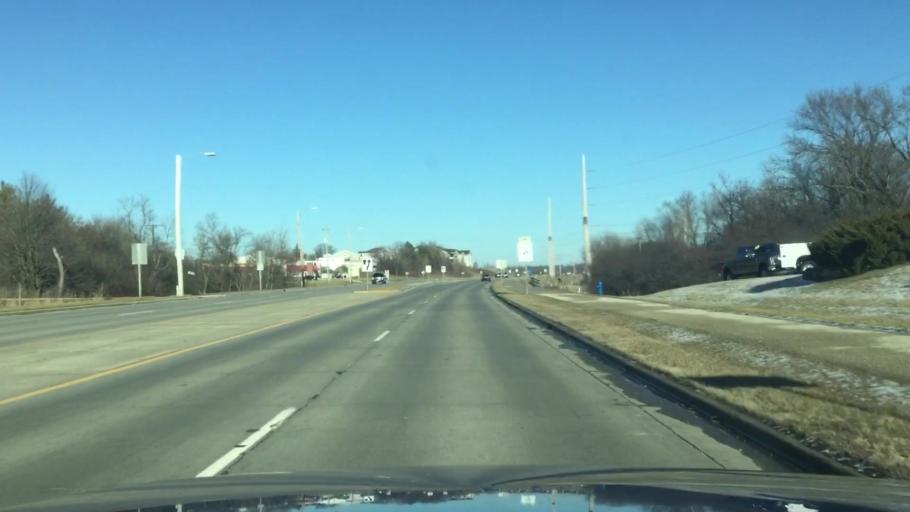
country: US
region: Wisconsin
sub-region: Racine County
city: Burlington
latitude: 42.6956
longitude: -88.2618
